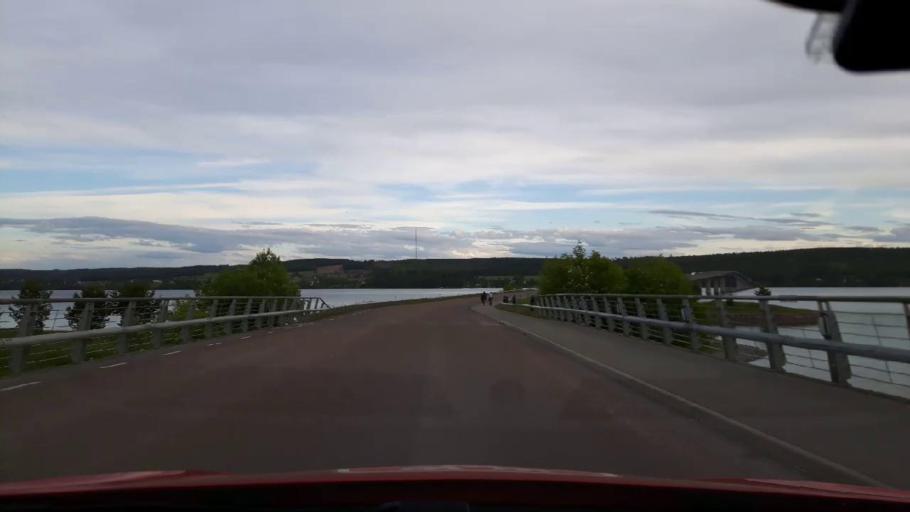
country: SE
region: Jaemtland
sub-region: OEstersunds Kommun
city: Ostersund
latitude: 63.1665
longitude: 14.6086
